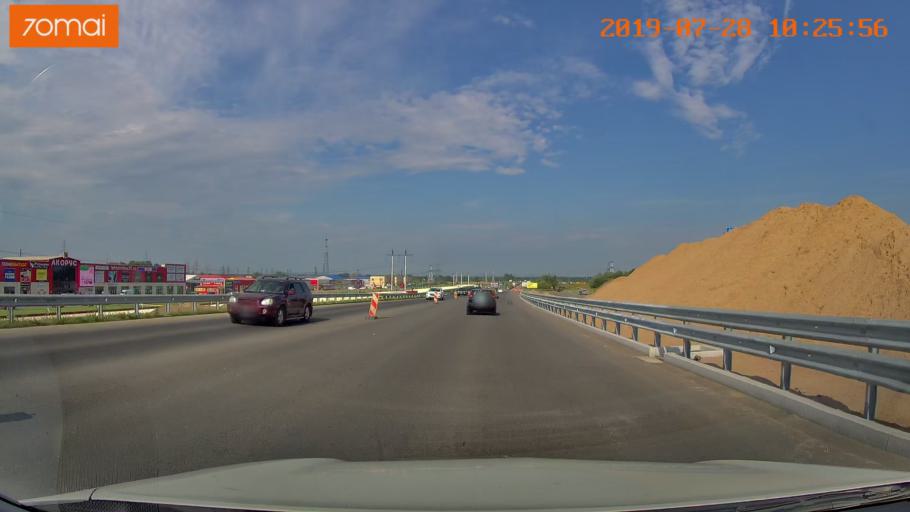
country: RU
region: Kaliningrad
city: Maloye Isakovo
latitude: 54.7680
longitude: 20.5346
